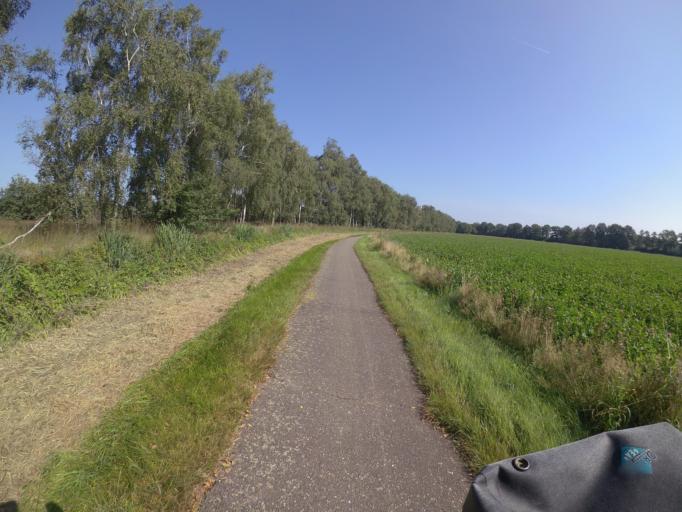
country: NL
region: North Brabant
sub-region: Gemeente Sint Anthonis
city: Sint Anthonis
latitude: 51.5176
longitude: 5.8282
